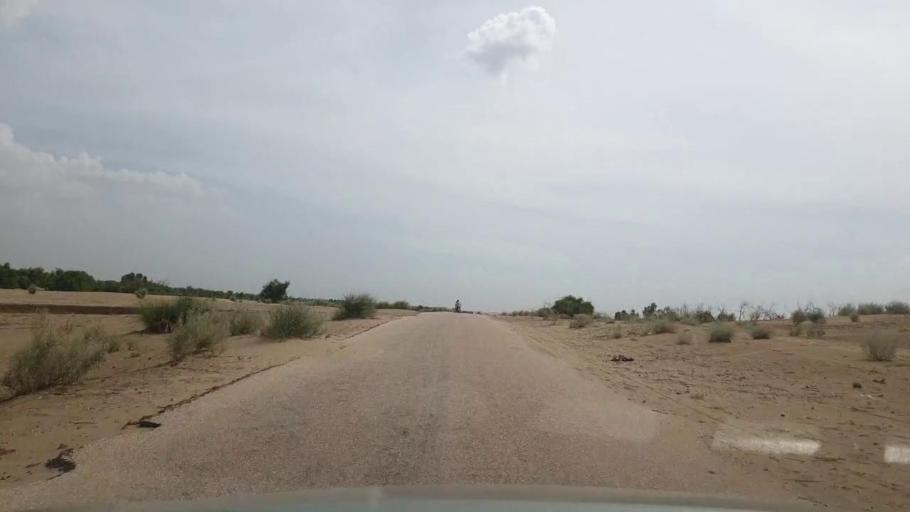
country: PK
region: Sindh
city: Kot Diji
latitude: 27.1505
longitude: 69.0324
